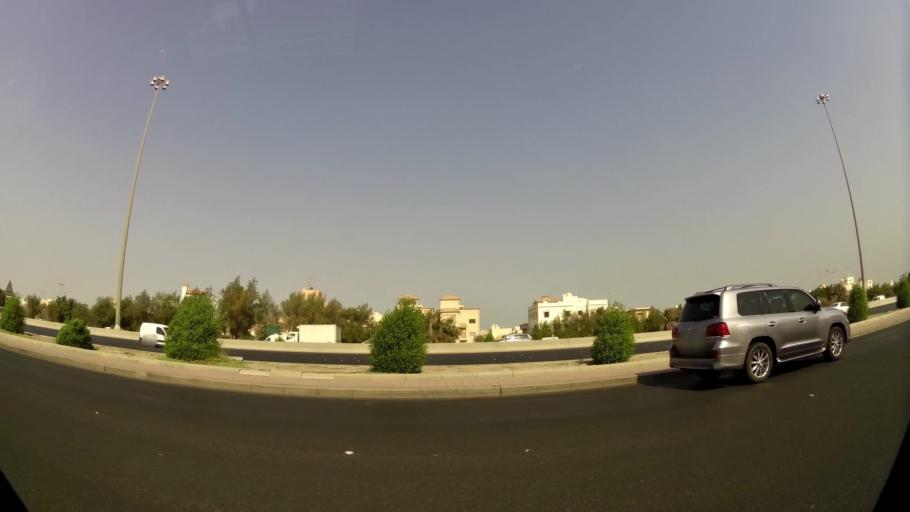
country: KW
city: Bayan
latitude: 29.3075
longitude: 48.0579
